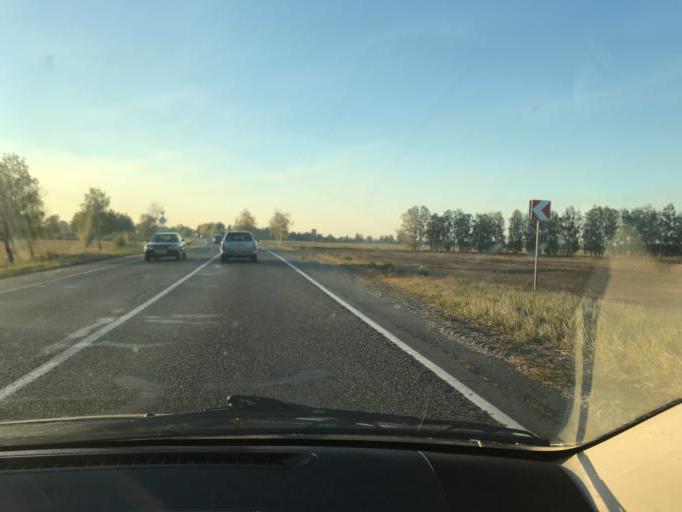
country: BY
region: Brest
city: Pinsk
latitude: 52.0718
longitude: 26.1742
